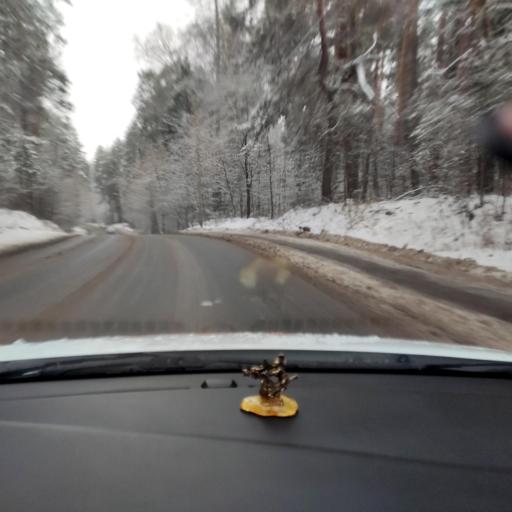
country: RU
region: Tatarstan
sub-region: Zelenodol'skiy Rayon
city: Zelenodolsk
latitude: 55.8632
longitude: 48.5350
